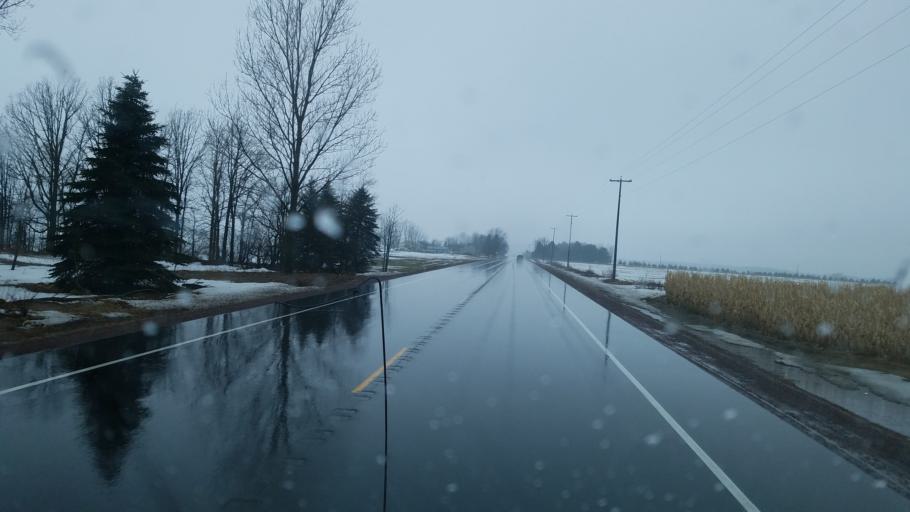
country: US
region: Wisconsin
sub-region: Marathon County
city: Spencer
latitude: 44.6563
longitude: -90.2834
